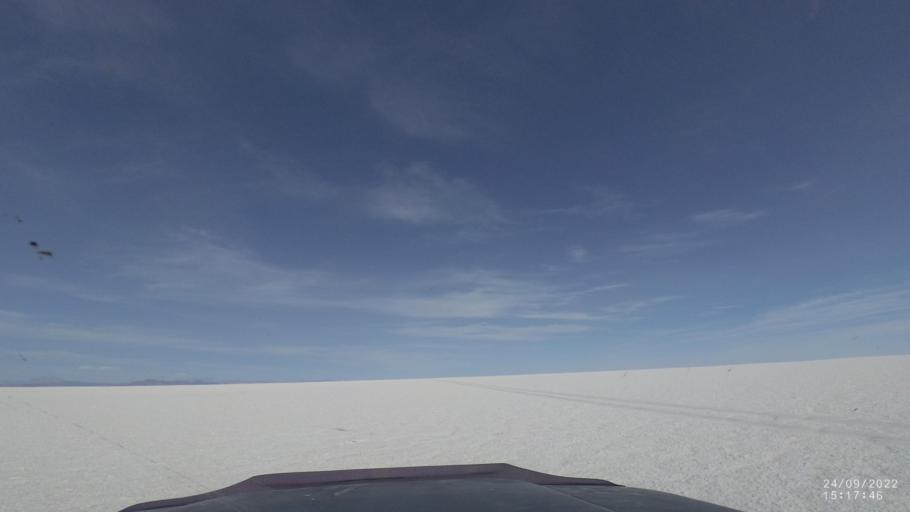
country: BO
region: Potosi
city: Colchani
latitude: -19.9917
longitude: -67.4245
